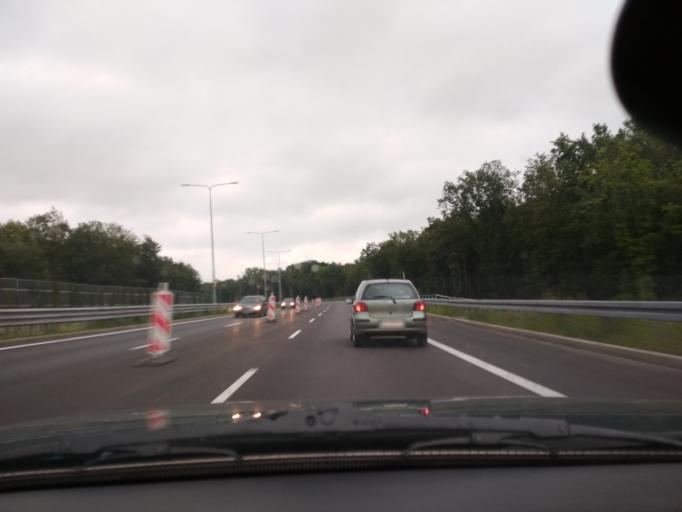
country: PL
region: Silesian Voivodeship
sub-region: Powiat gliwicki
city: Przyszowice
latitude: 50.2859
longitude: 18.7635
